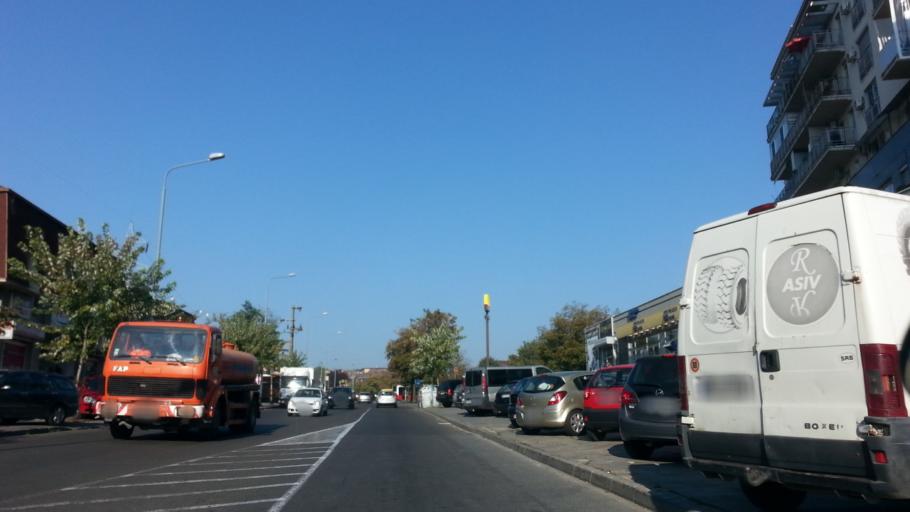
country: RS
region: Central Serbia
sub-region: Belgrade
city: Rakovica
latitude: 44.7429
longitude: 20.4268
